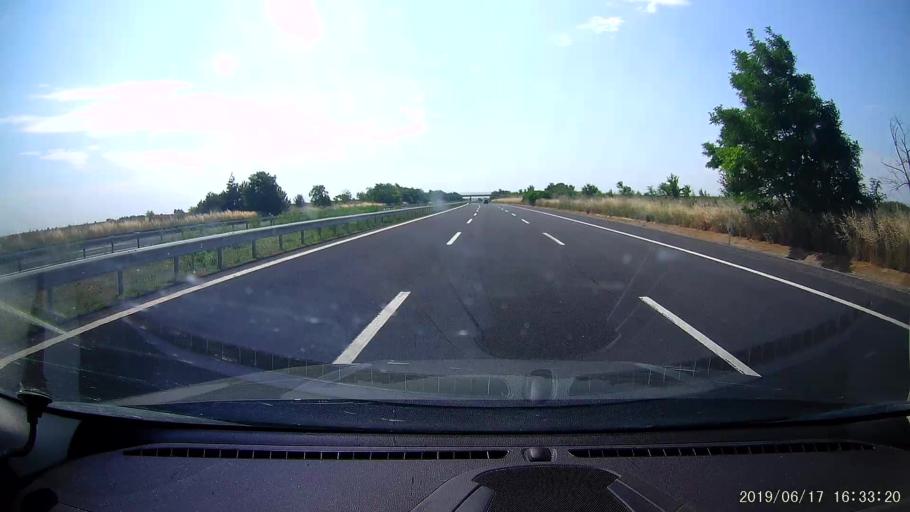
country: TR
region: Kirklareli
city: Buyukkaristiran
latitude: 41.3802
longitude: 27.5760
